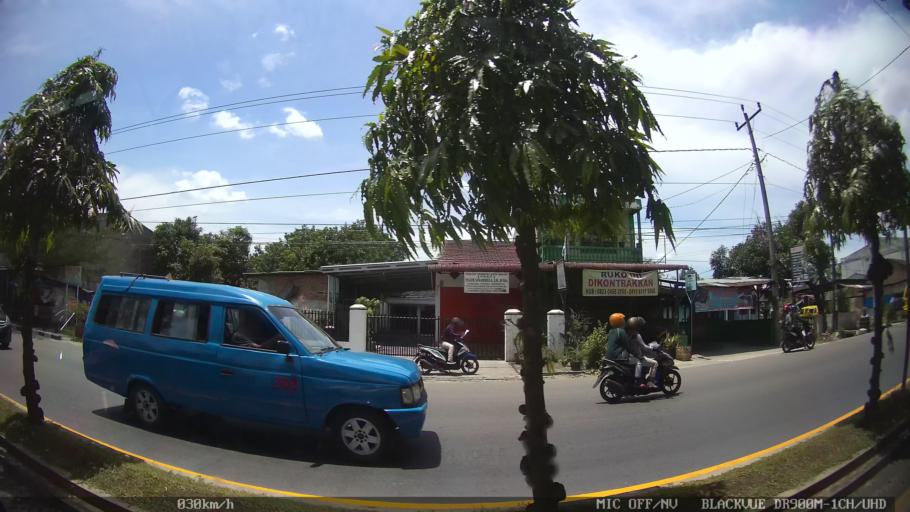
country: ID
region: North Sumatra
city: Binjai
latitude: 3.6086
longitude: 98.5029
